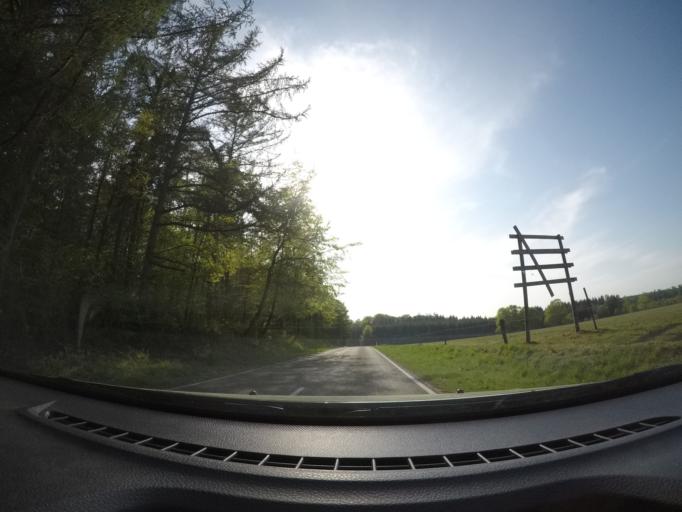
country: BE
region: Wallonia
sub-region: Province du Luxembourg
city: Tintigny
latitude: 49.6662
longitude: 5.5339
